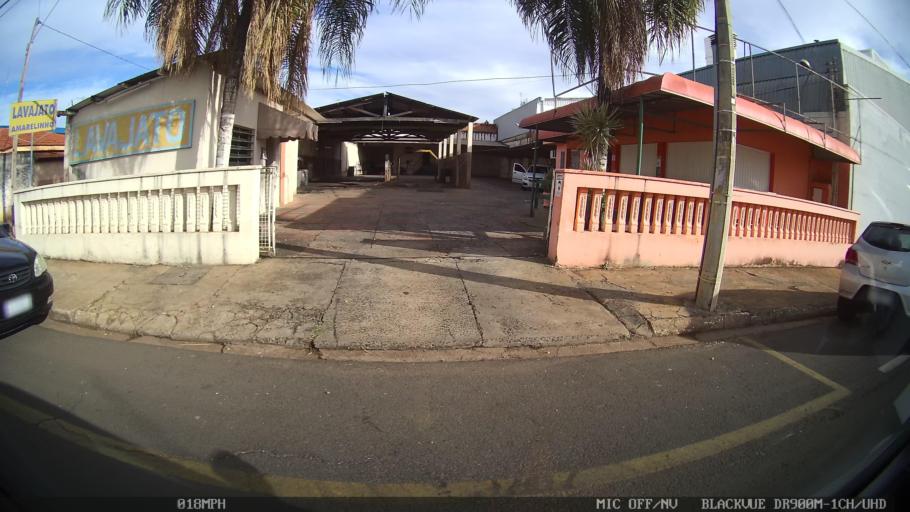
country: BR
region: Sao Paulo
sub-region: Catanduva
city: Catanduva
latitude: -21.1457
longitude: -48.9763
